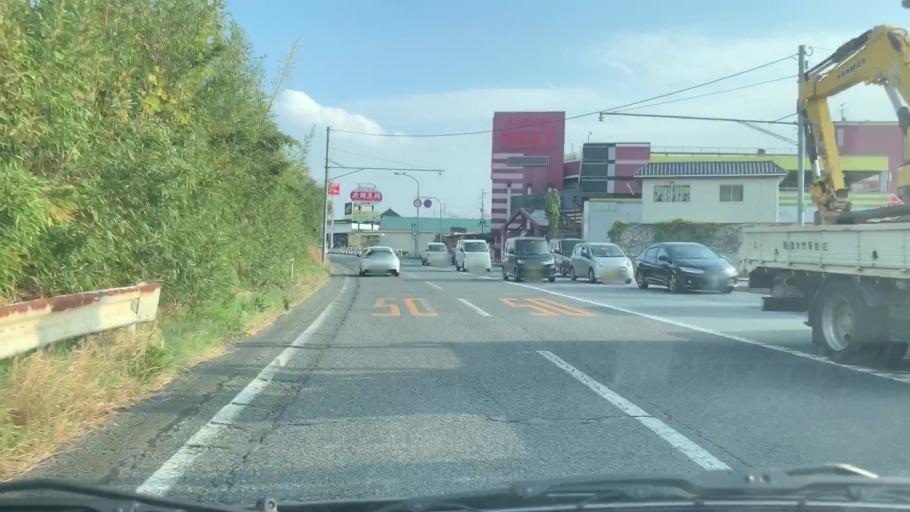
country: JP
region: Nagasaki
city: Sasebo
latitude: 33.1434
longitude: 129.7869
